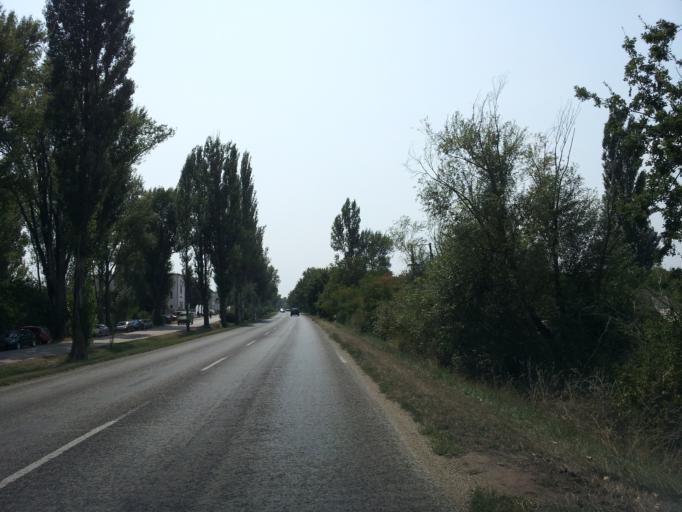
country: HU
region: Veszprem
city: Balatonfured
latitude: 46.9429
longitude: 17.8687
